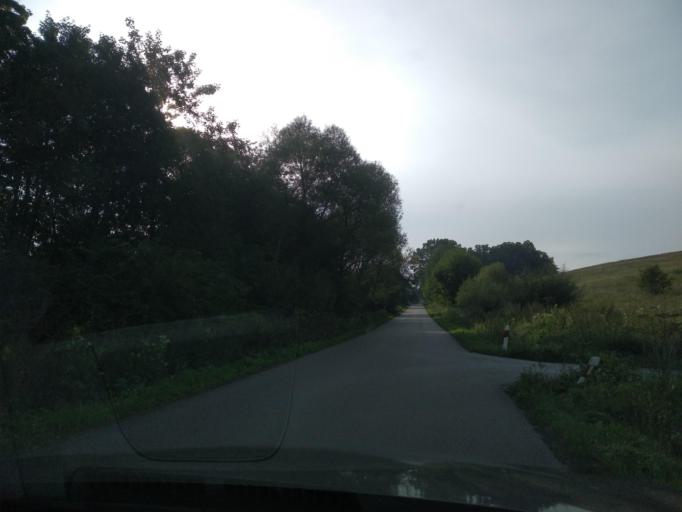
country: PL
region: Subcarpathian Voivodeship
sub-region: Powiat brzozowski
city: Dydnia
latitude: 49.6416
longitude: 22.2448
